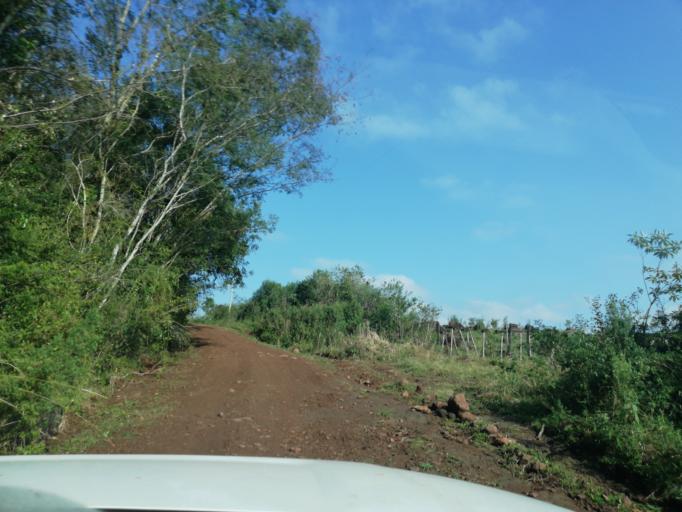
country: AR
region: Misiones
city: Cerro Azul
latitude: -27.5976
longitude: -55.5247
